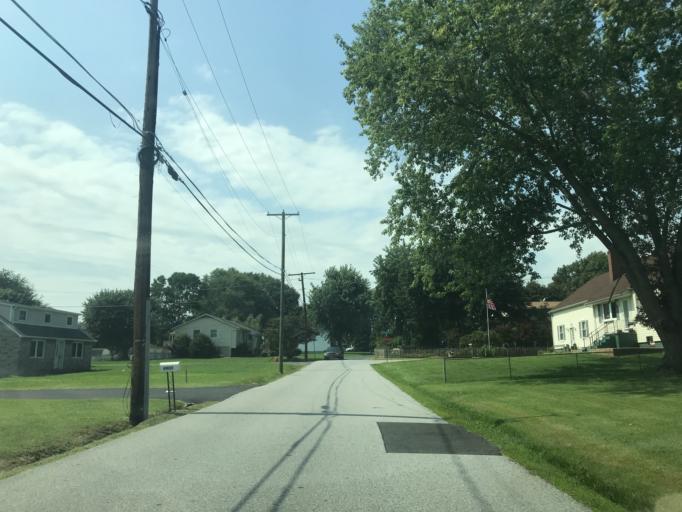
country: US
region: Maryland
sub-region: Baltimore County
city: Bowleys Quarters
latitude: 39.3743
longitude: -76.3635
